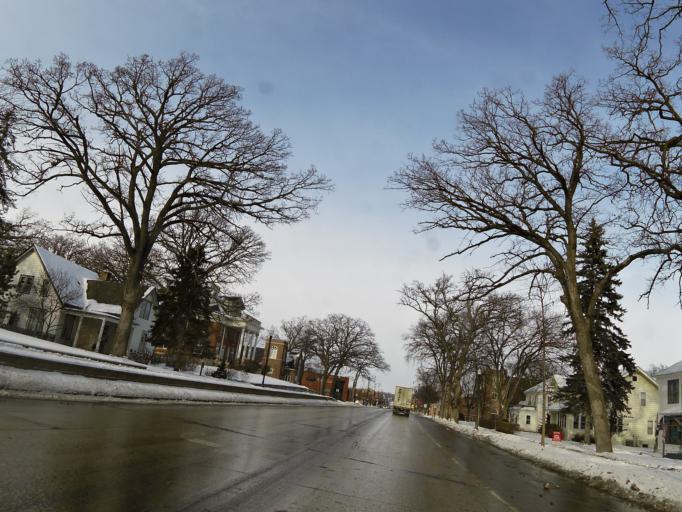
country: US
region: Minnesota
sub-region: McLeod County
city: Hutchinson
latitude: 44.8867
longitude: -94.3692
